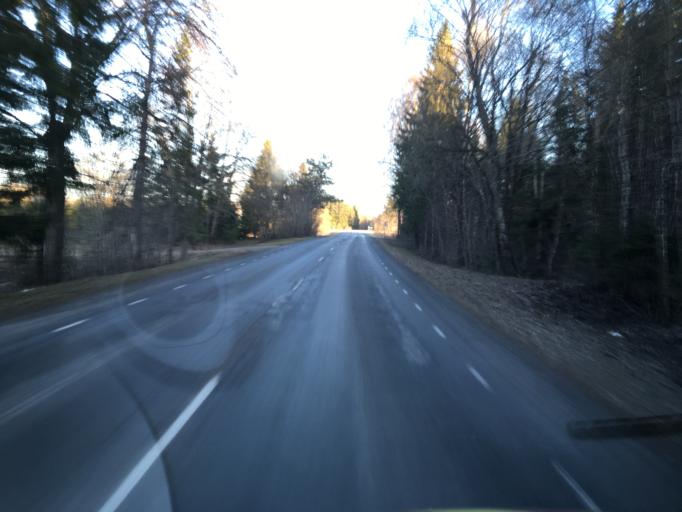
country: EE
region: Raplamaa
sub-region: Rapla vald
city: Rapla
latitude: 59.0666
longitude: 24.9225
